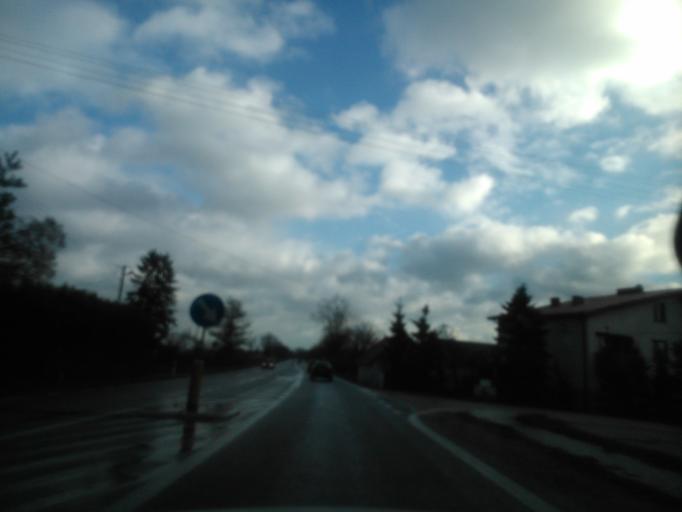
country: PL
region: Masovian Voivodeship
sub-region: Powiat sierpecki
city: Rosciszewo
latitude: 52.8288
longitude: 19.7556
